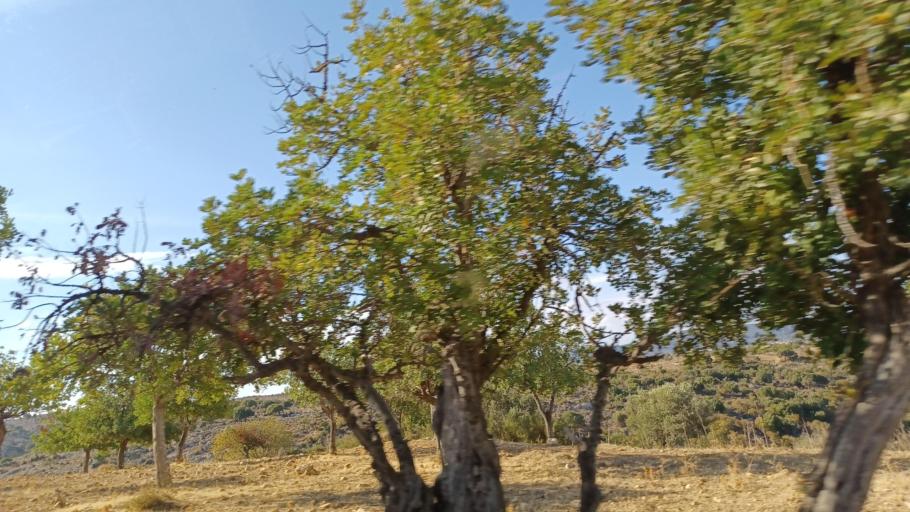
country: CY
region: Pafos
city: Polis
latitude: 35.0119
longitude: 32.3926
